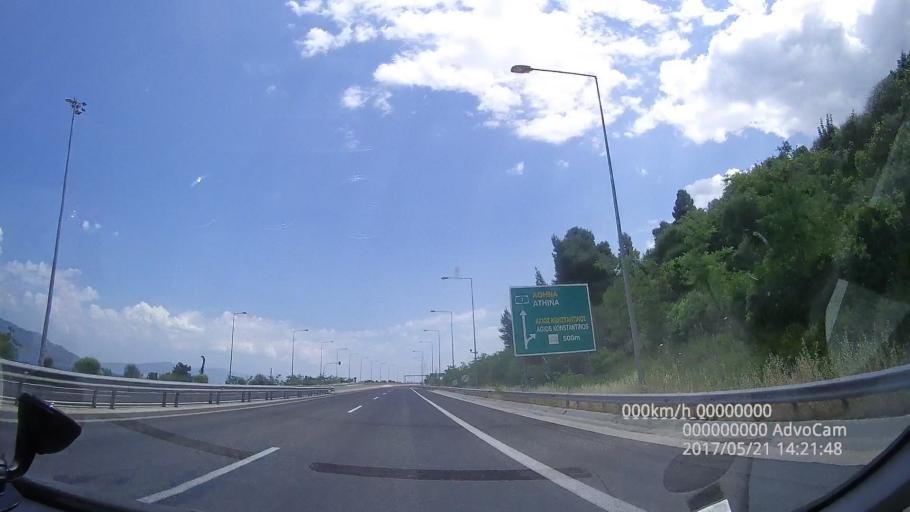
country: GR
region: Central Greece
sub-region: Nomos Fthiotidos
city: Ayios Konstandinos
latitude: 38.7662
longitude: 22.8331
